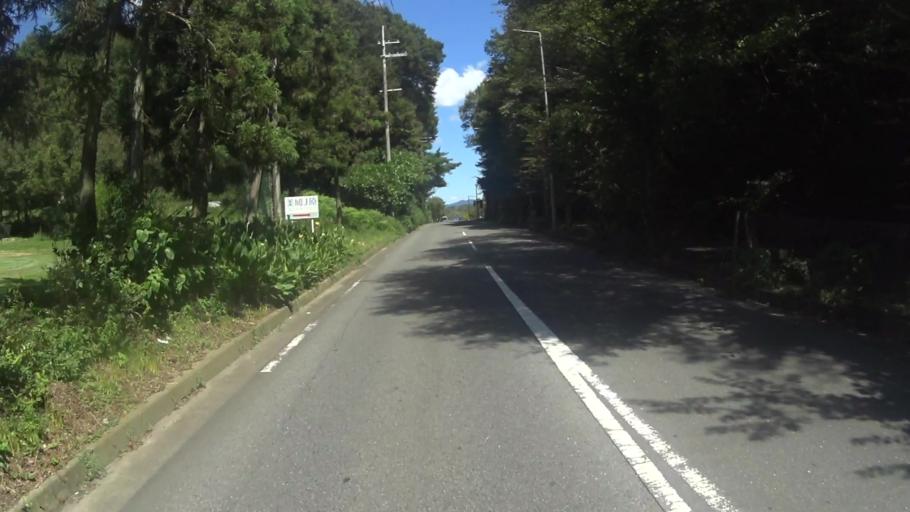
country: JP
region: Nara
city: Nara-shi
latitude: 34.7124
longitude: 135.8319
